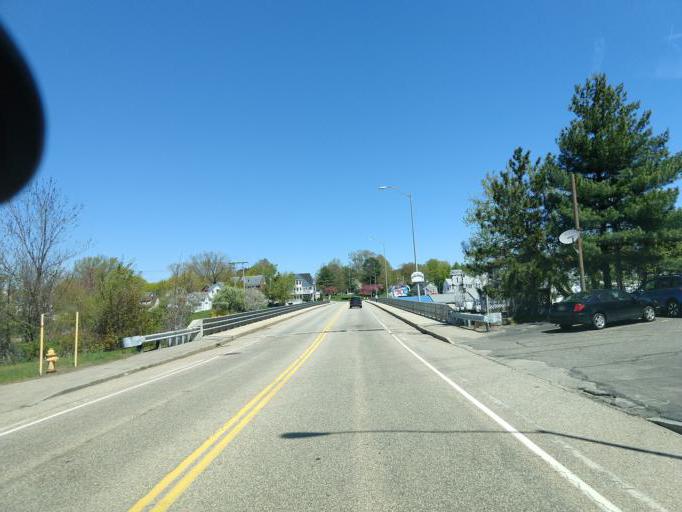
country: US
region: New Hampshire
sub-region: Rockingham County
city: Portsmouth
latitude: 43.0825
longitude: -70.7514
